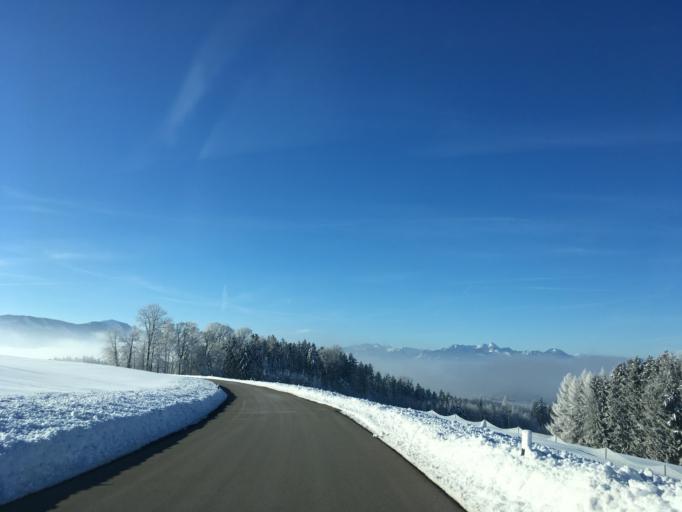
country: DE
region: Bavaria
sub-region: Upper Bavaria
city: Bad Endorf
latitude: 47.8704
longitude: 12.2898
